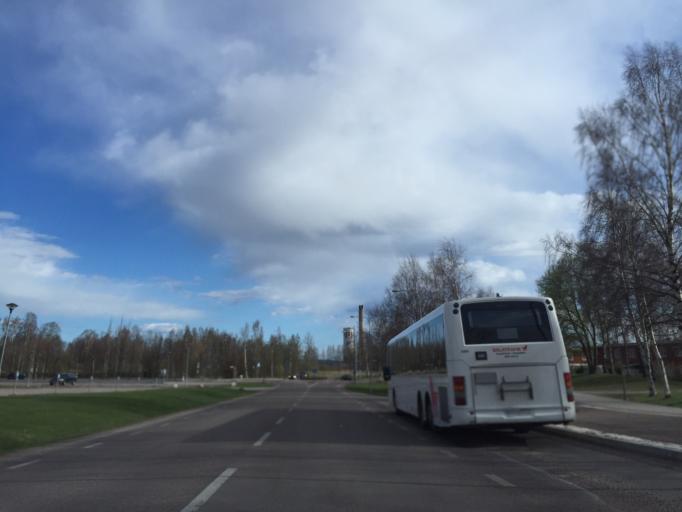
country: SE
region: Dalarna
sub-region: Borlange Kommun
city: Borlaenge
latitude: 60.4833
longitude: 15.4067
